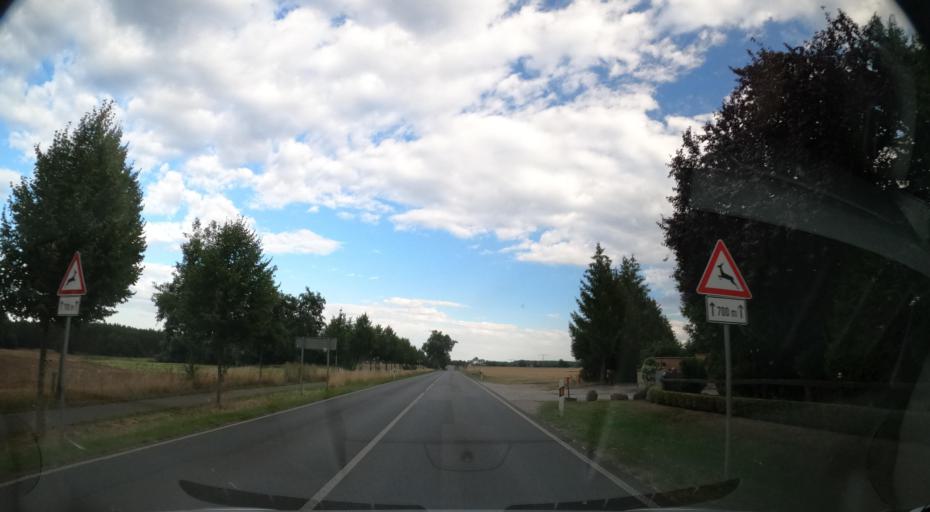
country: DE
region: Mecklenburg-Vorpommern
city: Viereck
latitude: 53.5029
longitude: 14.0427
